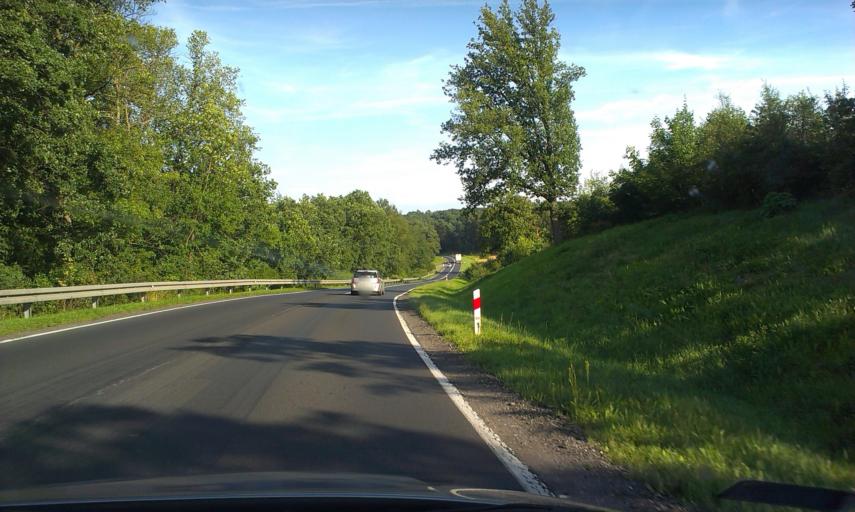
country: PL
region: Kujawsko-Pomorskie
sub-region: Powiat bydgoski
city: Sicienko
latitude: 53.1642
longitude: 17.7888
